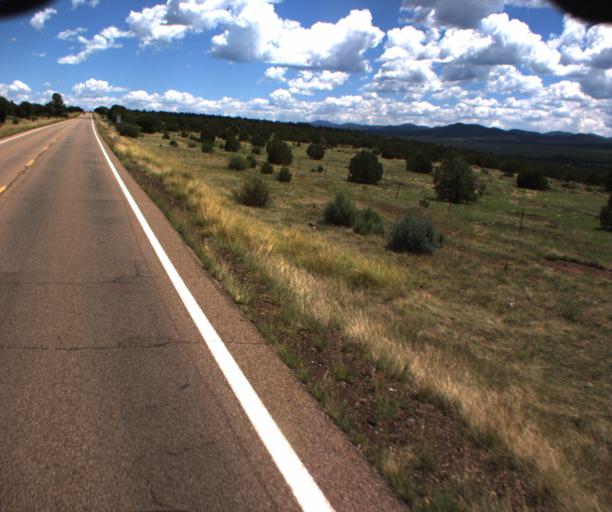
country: US
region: Arizona
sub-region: Navajo County
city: White Mountain Lake
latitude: 34.2847
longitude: -109.8189
